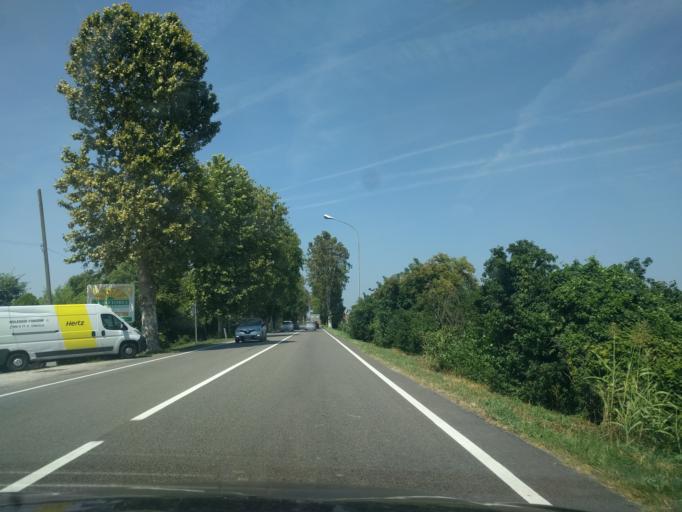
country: IT
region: Veneto
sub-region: Provincia di Padova
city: Stanghella
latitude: 45.1399
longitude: 11.7570
